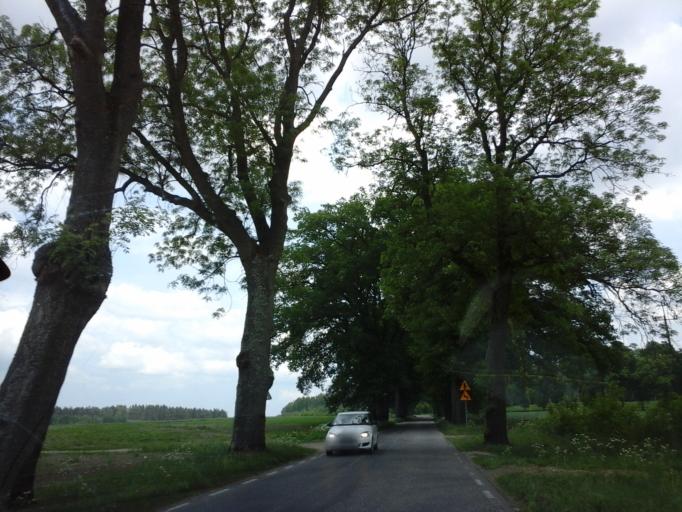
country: PL
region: West Pomeranian Voivodeship
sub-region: Powiat drawski
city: Kalisz Pomorski
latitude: 53.2606
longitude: 15.8598
